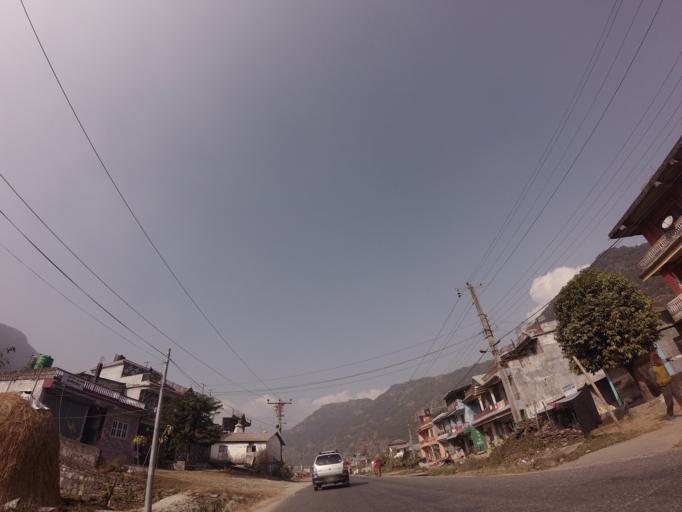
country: NP
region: Western Region
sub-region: Gandaki Zone
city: Pokhara
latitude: 28.2809
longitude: 83.9282
